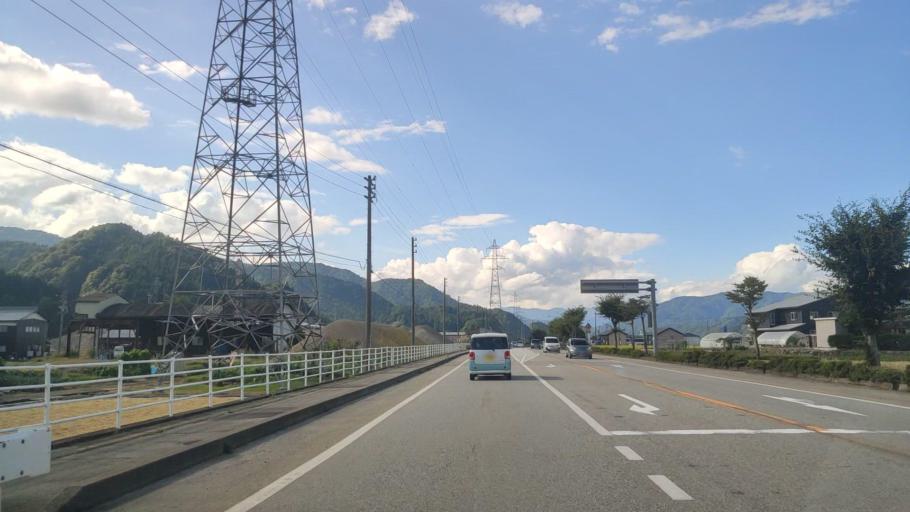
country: JP
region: Gifu
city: Takayama
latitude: 36.2212
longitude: 137.1925
